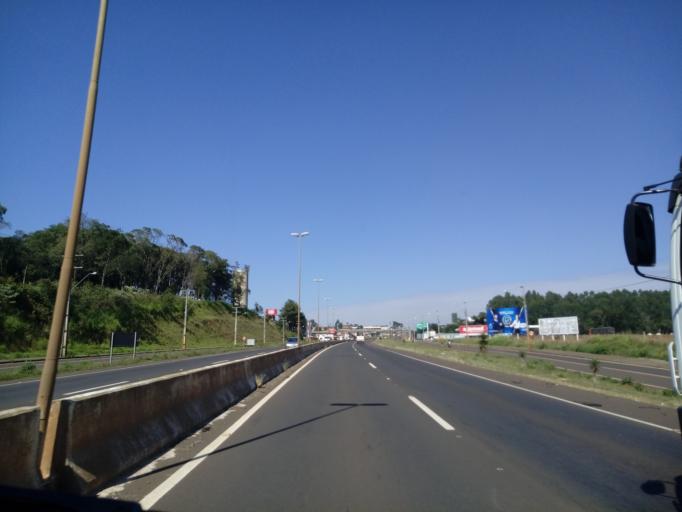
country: BR
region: Santa Catarina
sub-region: Chapeco
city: Chapeco
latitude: -27.0296
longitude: -52.6337
